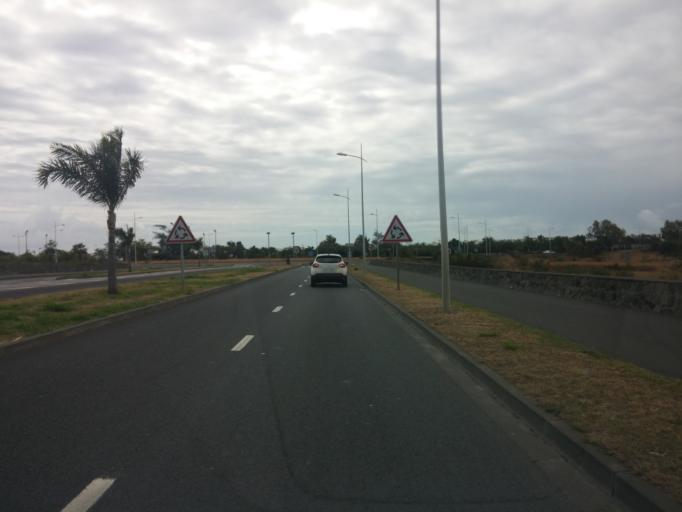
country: RE
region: Reunion
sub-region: Reunion
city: Le Port
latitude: -20.9540
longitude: 55.2945
